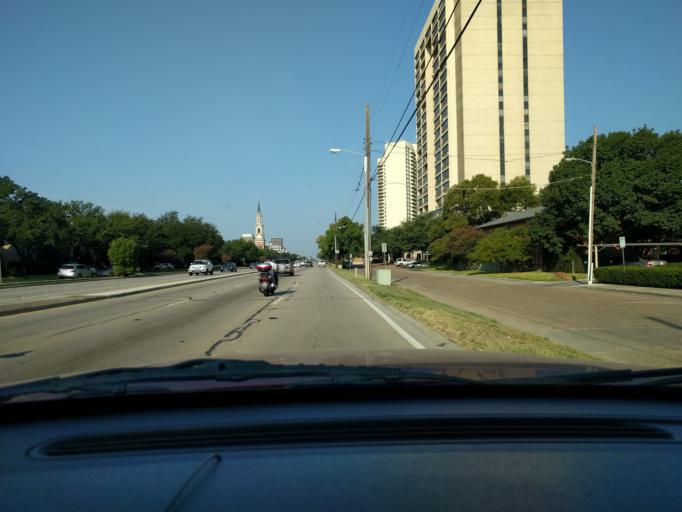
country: US
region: Texas
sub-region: Dallas County
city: University Park
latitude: 32.8657
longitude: -96.7957
